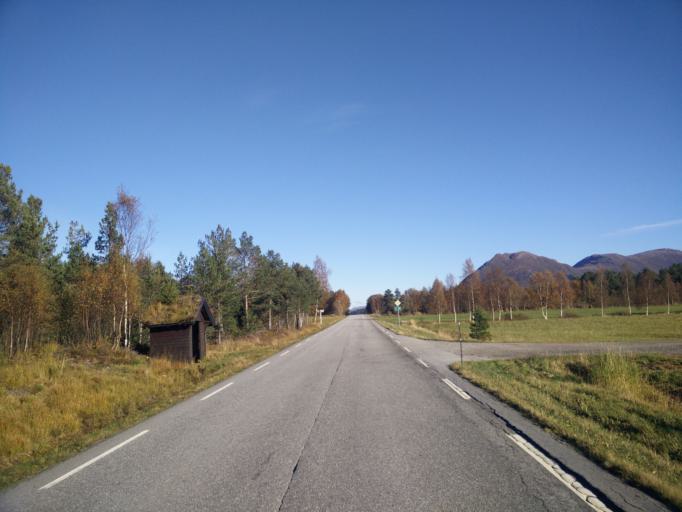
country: NO
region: More og Romsdal
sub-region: Halsa
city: Liaboen
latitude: 63.1227
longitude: 8.3386
